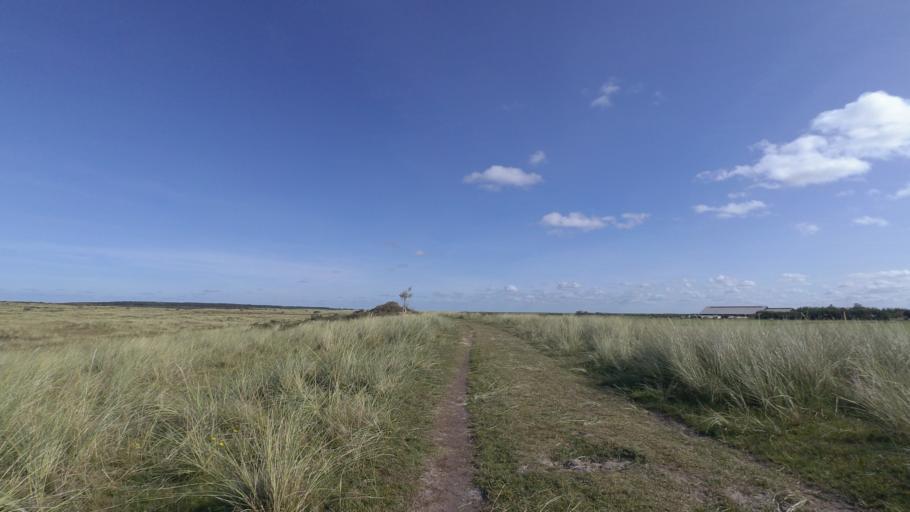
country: NL
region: Friesland
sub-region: Gemeente Ameland
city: Nes
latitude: 53.4508
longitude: 5.7239
